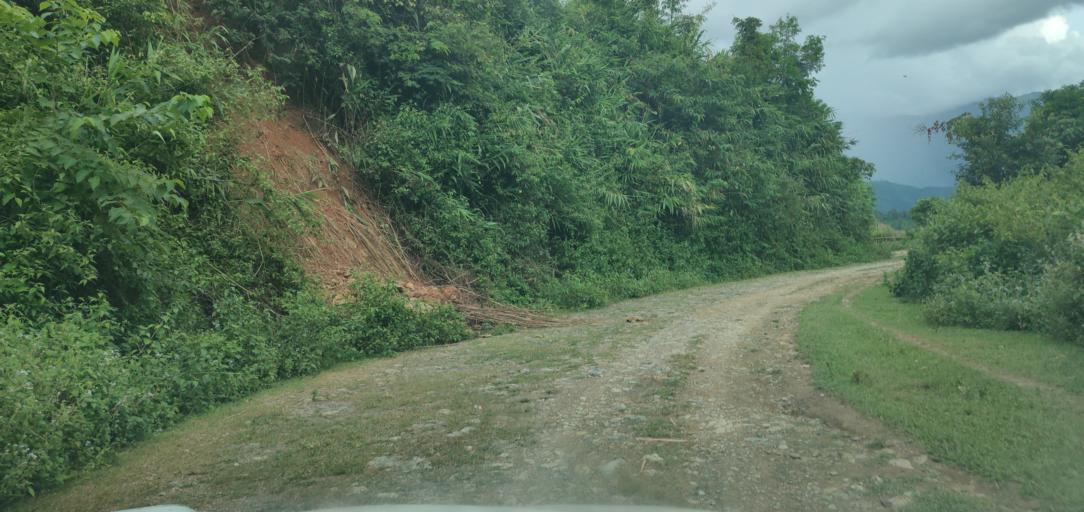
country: LA
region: Phongsali
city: Phongsali
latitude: 21.4464
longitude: 102.3038
